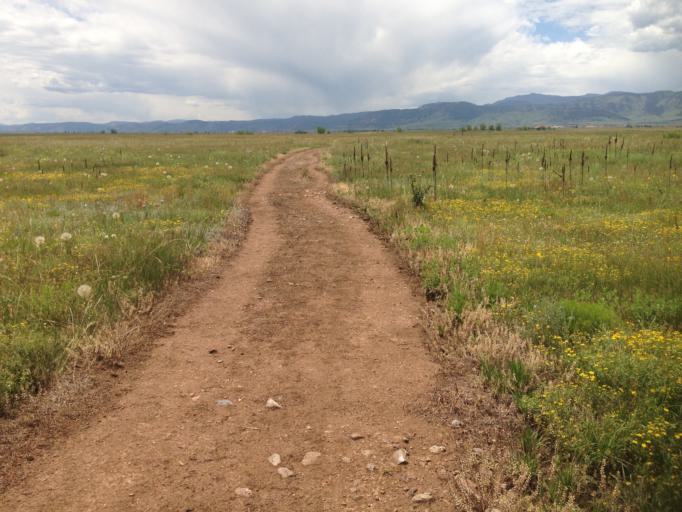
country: US
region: Colorado
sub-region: Boulder County
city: Superior
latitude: 39.9095
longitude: -105.1902
